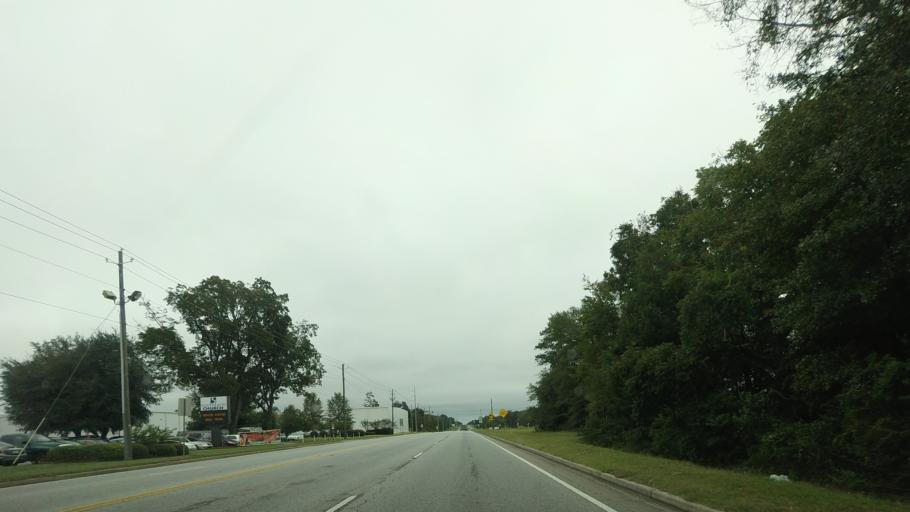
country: US
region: Georgia
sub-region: Lowndes County
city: Valdosta
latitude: 30.8420
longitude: -83.2487
